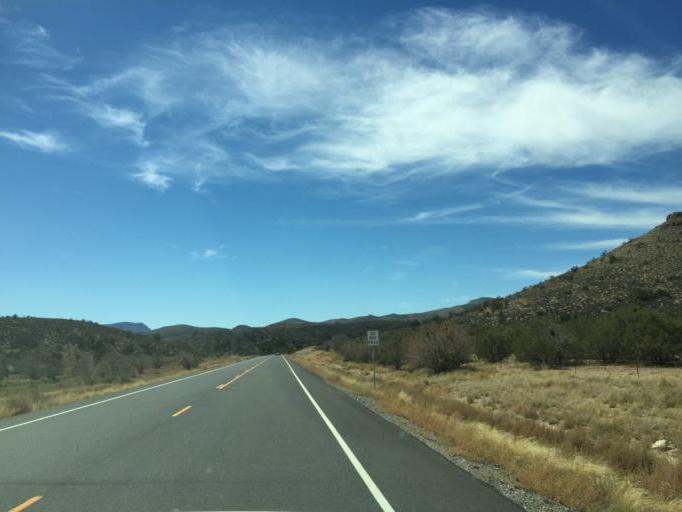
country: US
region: Arizona
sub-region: Mohave County
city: Meadview
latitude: 35.9204
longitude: -113.9180
